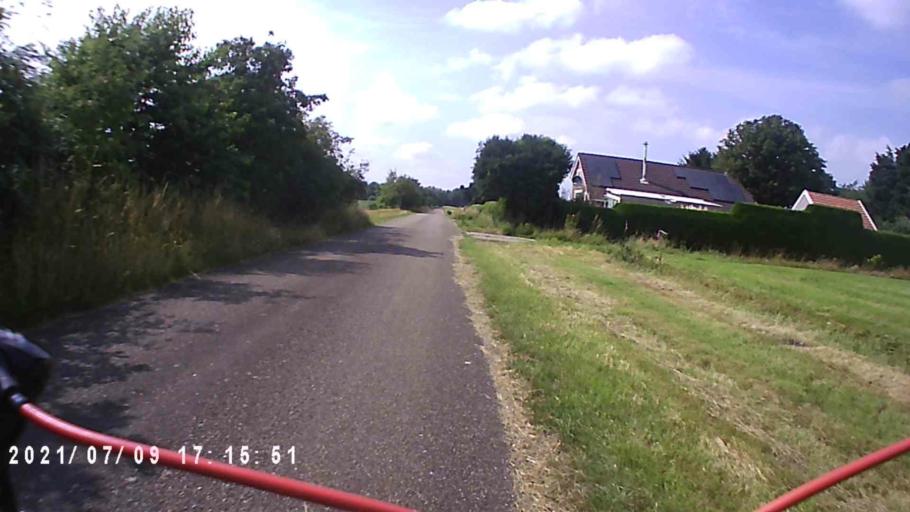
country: DE
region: Lower Saxony
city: Rhede
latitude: 53.0888
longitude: 7.1832
